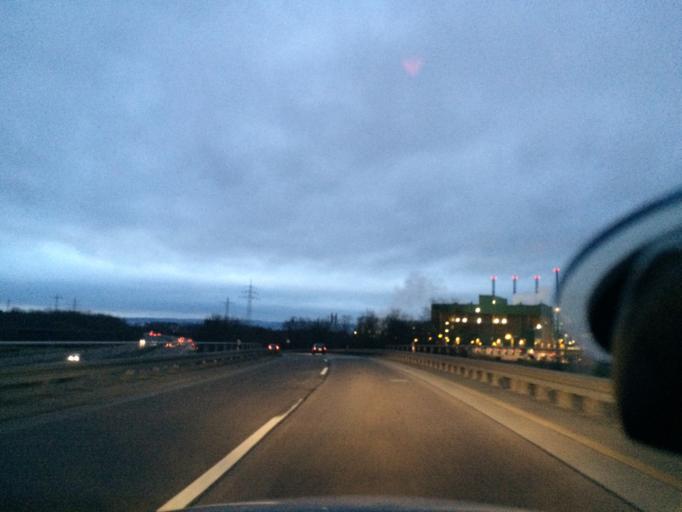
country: DE
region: Hesse
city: Kelsterbach
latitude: 50.0766
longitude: 8.5387
